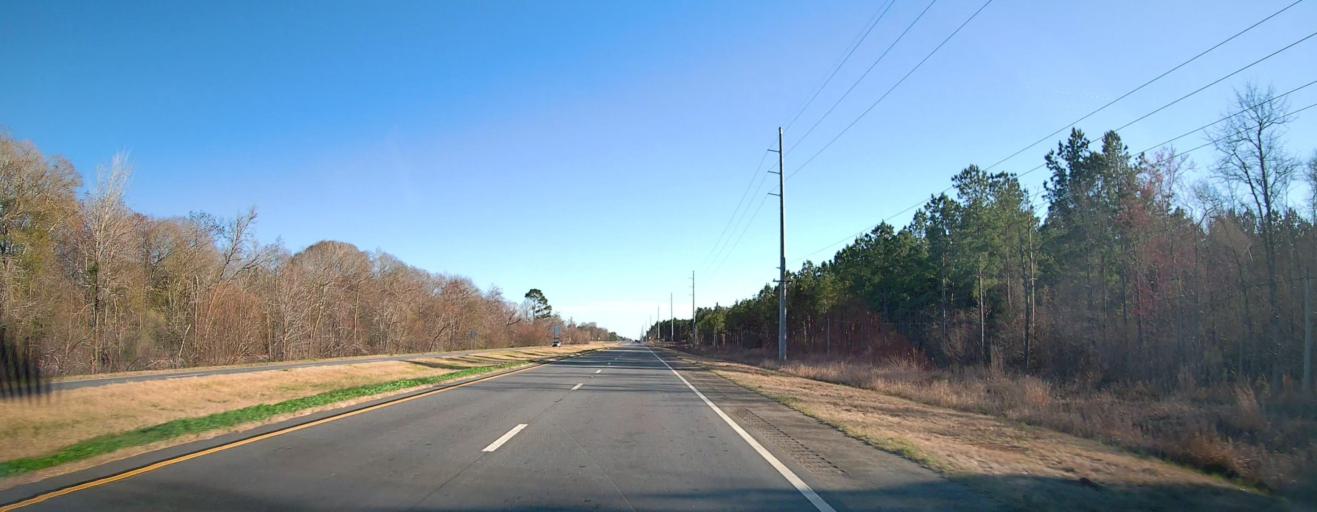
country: US
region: Georgia
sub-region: Lee County
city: Leesburg
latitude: 31.8801
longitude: -84.2426
